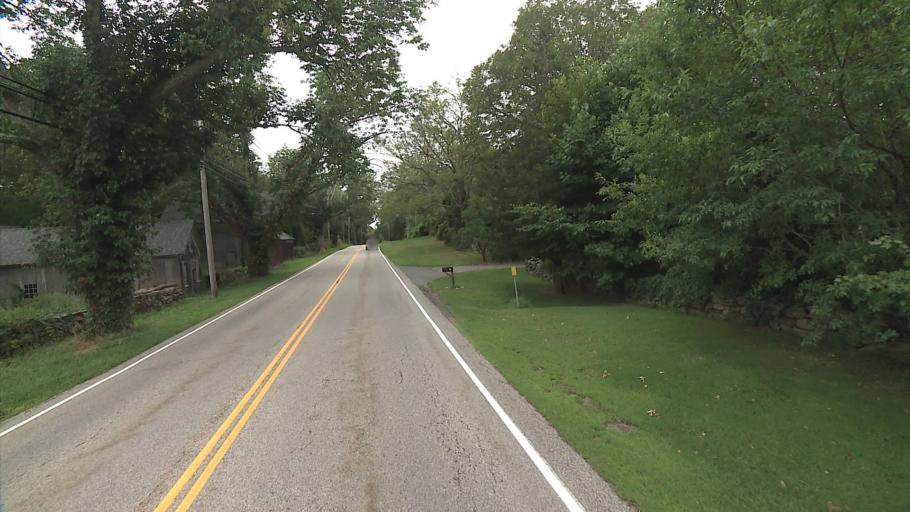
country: US
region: Connecticut
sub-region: Middlesex County
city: Essex Village
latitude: 41.3607
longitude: -72.3428
